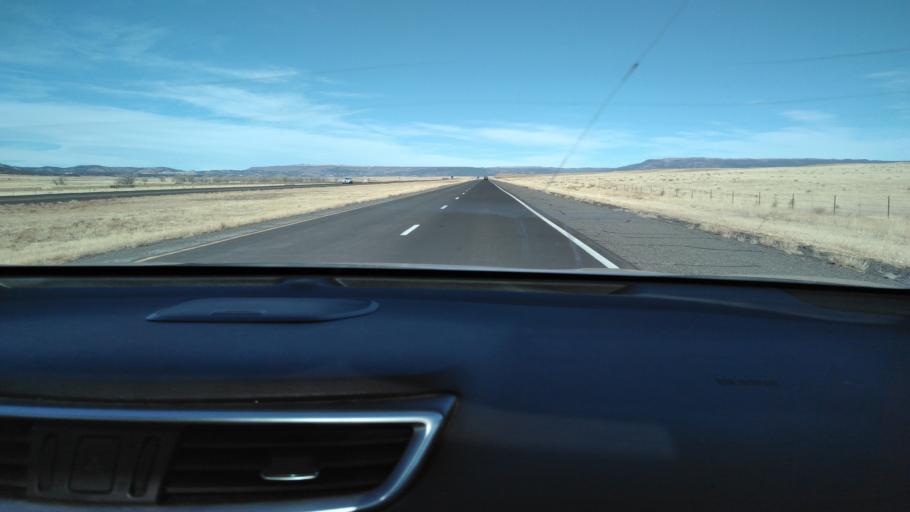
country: US
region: New Mexico
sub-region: Colfax County
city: Raton
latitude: 36.7381
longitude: -104.4555
